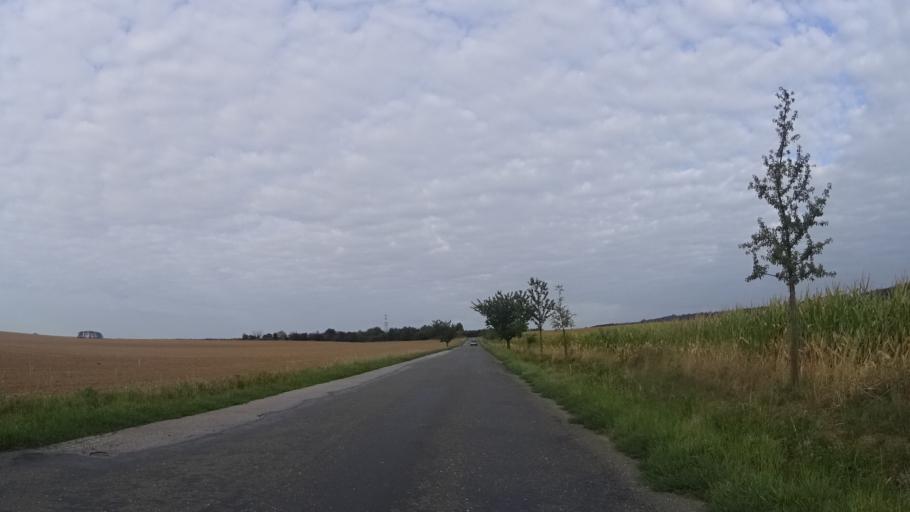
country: CZ
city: Stezery
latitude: 50.2126
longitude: 15.7427
